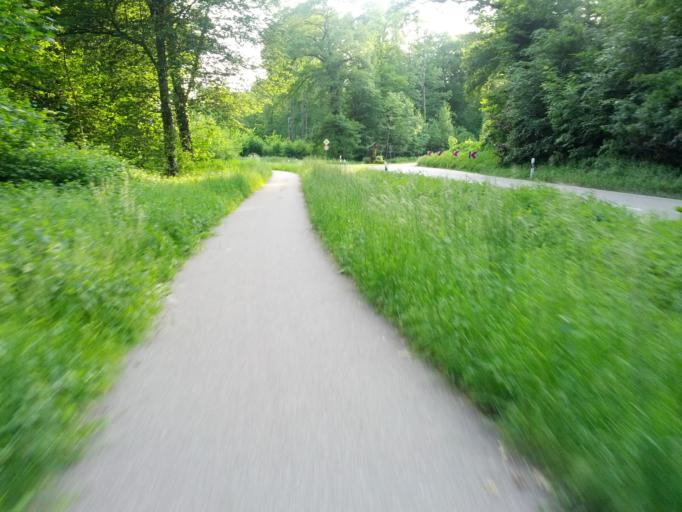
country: DE
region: Baden-Wuerttemberg
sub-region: Freiburg Region
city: Umkirch
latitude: 48.0280
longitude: 7.7549
